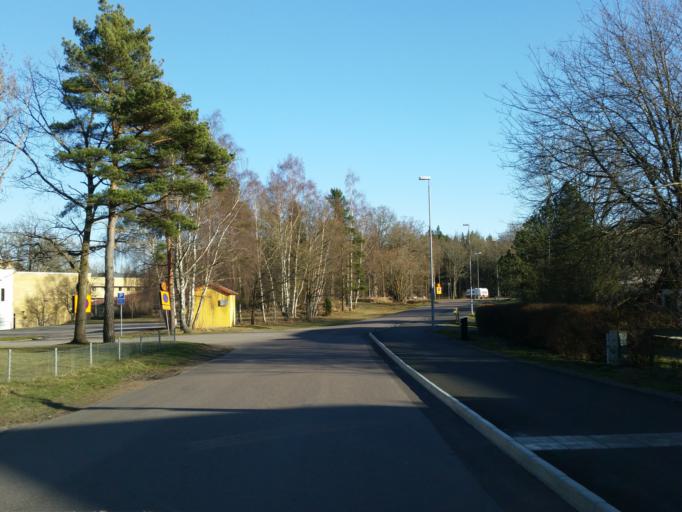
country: SE
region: Kalmar
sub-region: Oskarshamns Kommun
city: Oskarshamn
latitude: 57.2637
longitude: 16.4192
